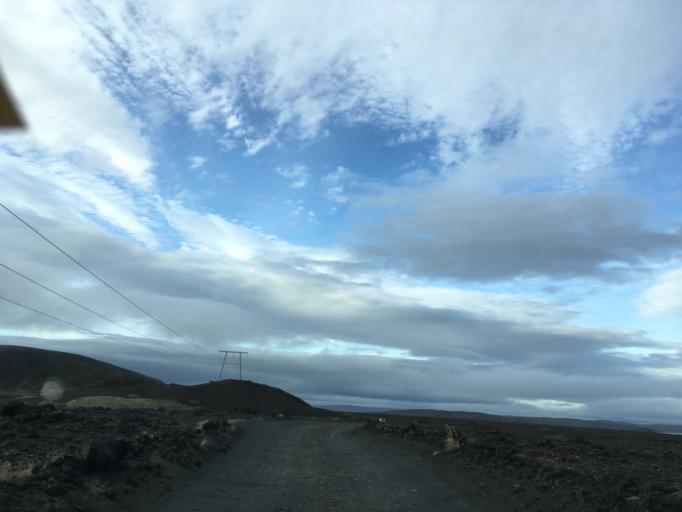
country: IS
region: South
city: Vestmannaeyjar
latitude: 64.1242
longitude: -19.1185
